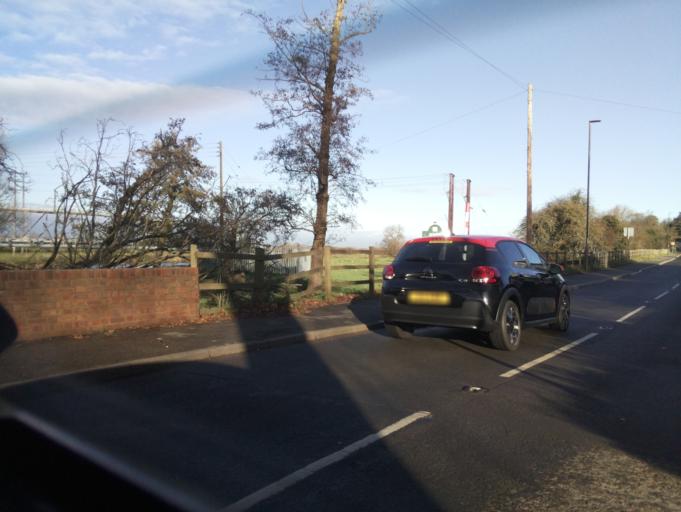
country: GB
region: England
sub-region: Staffordshire
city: Burton upon Trent
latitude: 52.8155
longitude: -1.6097
